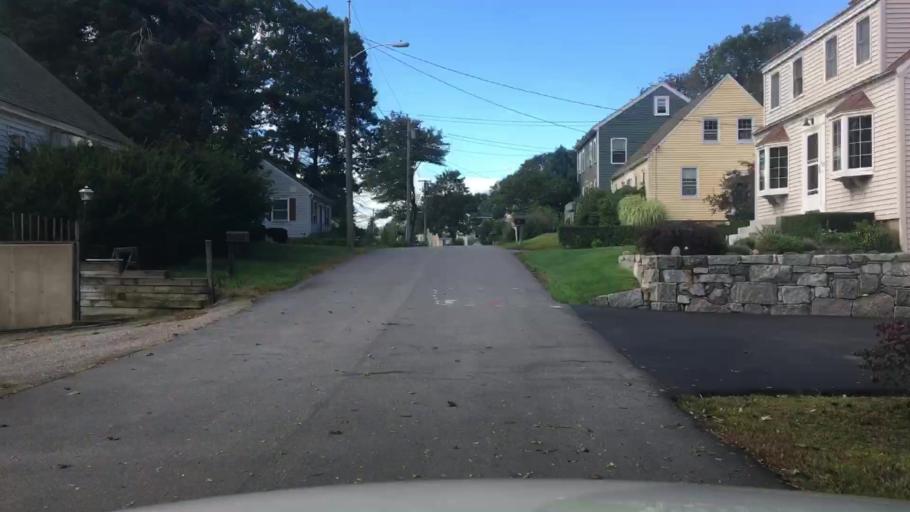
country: US
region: Maine
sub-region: York County
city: Kittery
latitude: 43.0886
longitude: -70.7270
